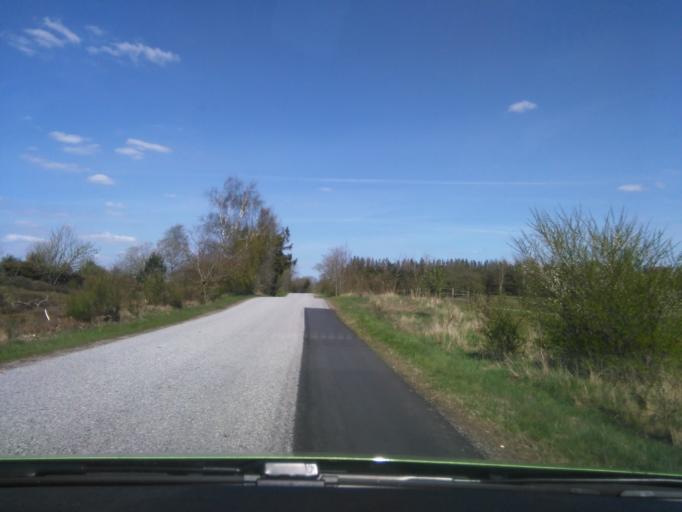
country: DK
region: Central Jutland
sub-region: Viborg Kommune
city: Viborg
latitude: 56.3810
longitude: 9.3020
